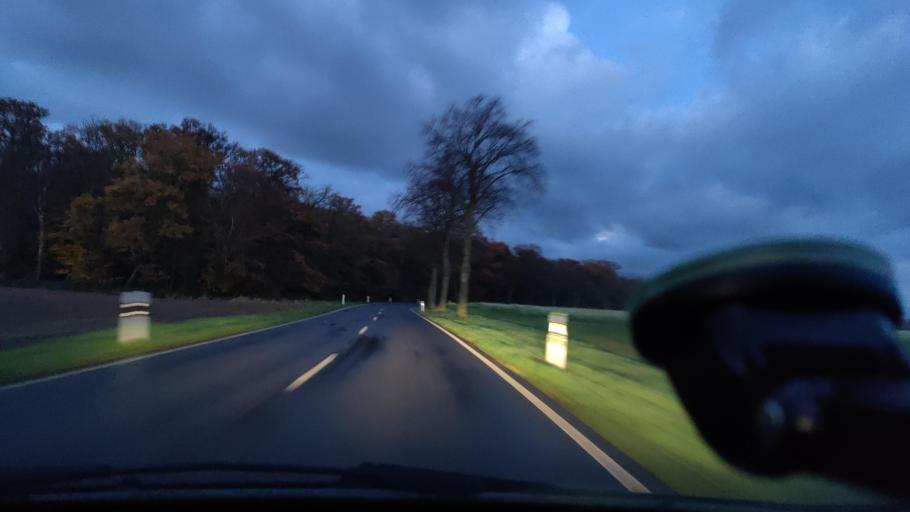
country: DE
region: North Rhine-Westphalia
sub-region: Regierungsbezirk Dusseldorf
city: Kevelaer
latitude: 51.6071
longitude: 6.2930
